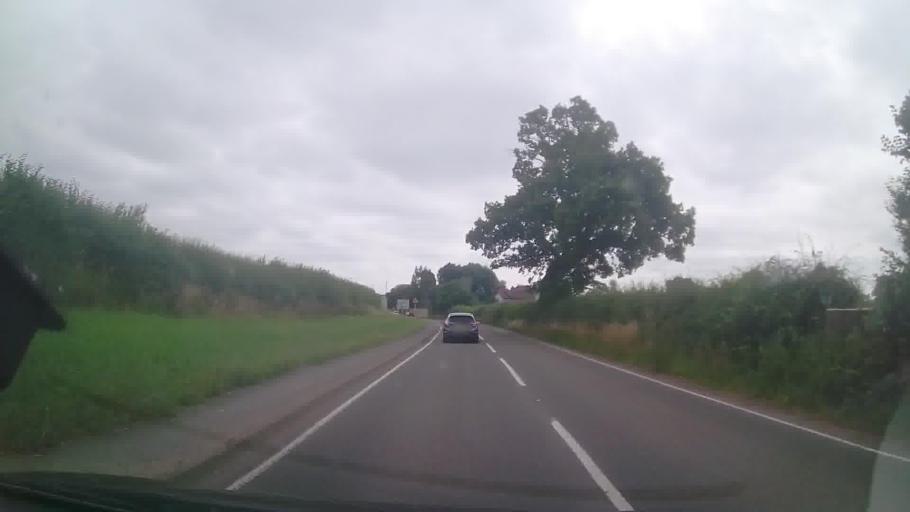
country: GB
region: England
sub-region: Leicestershire
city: Desford
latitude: 52.6355
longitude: -1.2805
